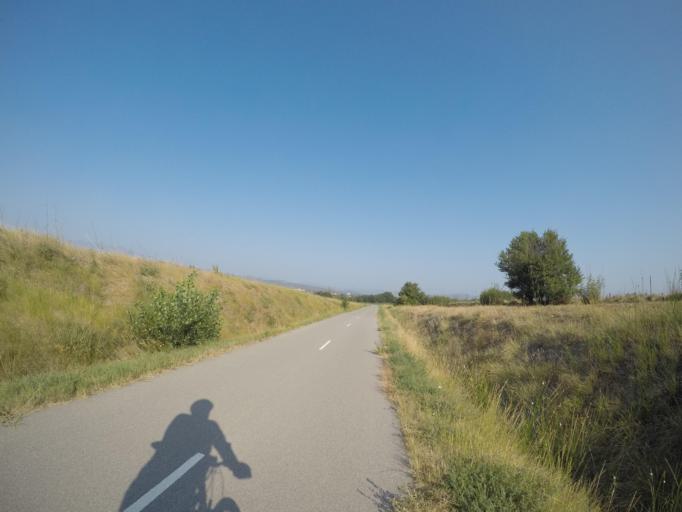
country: FR
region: Languedoc-Roussillon
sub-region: Departement des Pyrenees-Orientales
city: Trouillas
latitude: 42.6227
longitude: 2.7934
